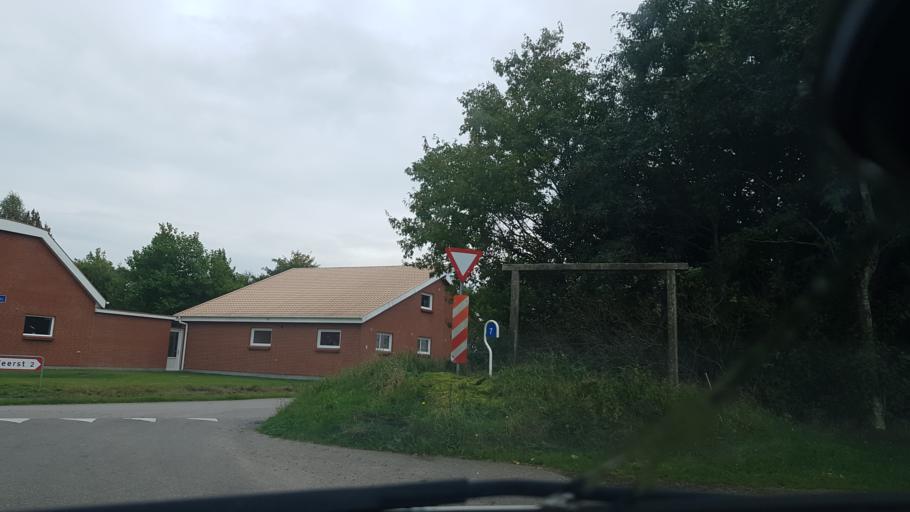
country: DK
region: South Denmark
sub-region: Vejle Kommune
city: Egtved
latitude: 55.5801
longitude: 9.2291
